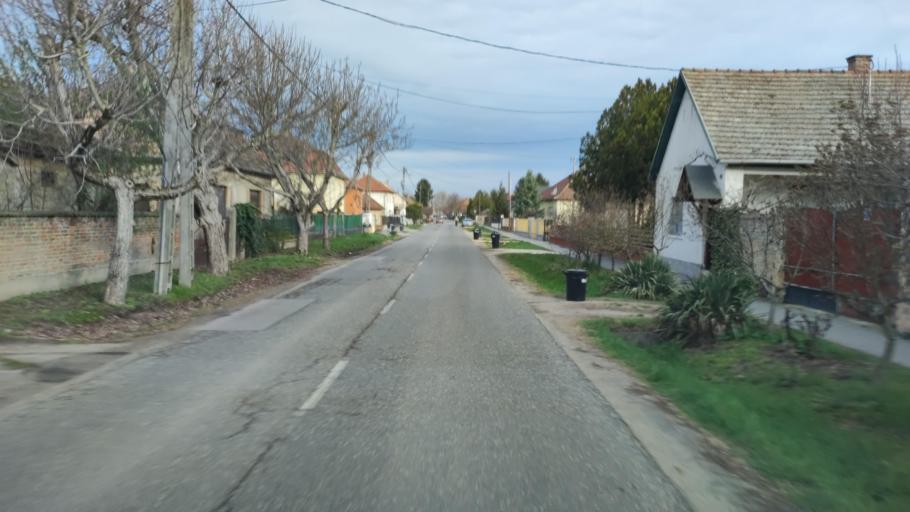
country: HU
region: Pest
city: Toekoel
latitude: 47.3181
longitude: 18.9696
